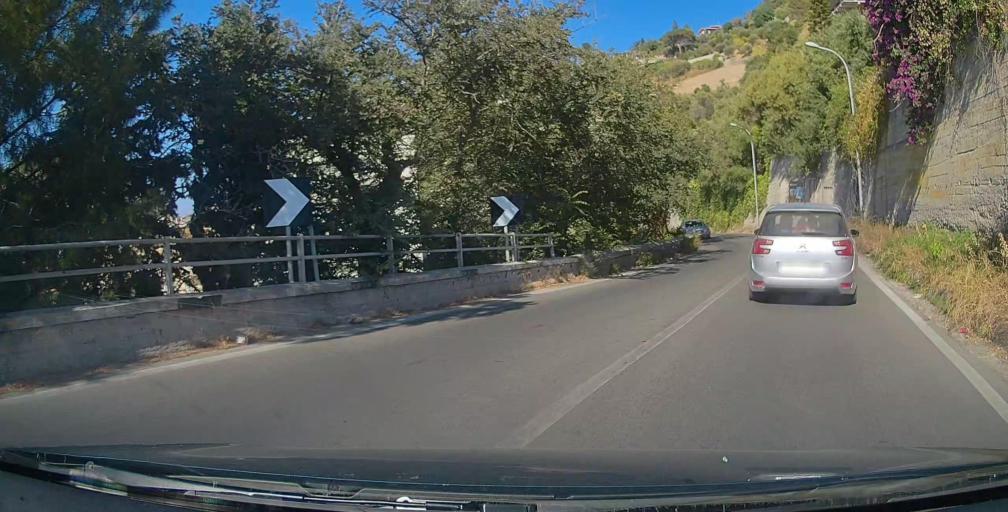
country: IT
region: Sicily
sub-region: Messina
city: Capo d'Orlando
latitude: 38.1589
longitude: 14.7486
